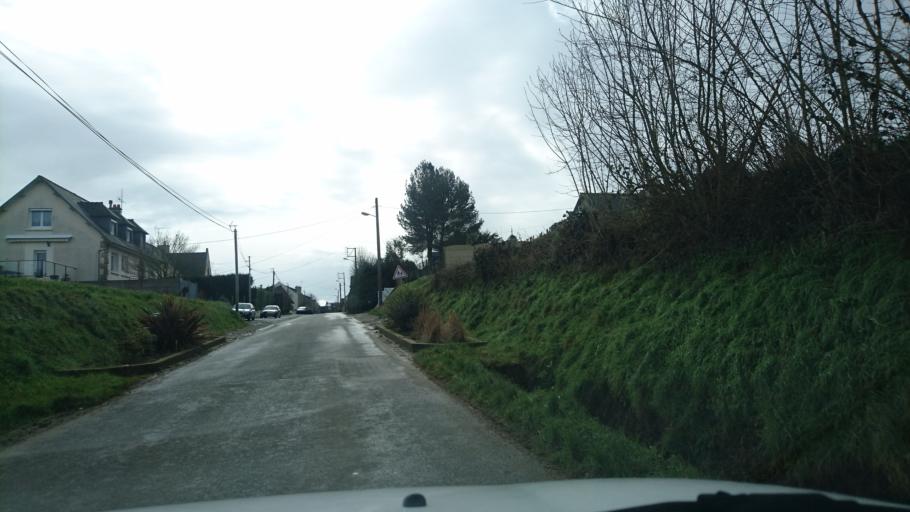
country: FR
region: Brittany
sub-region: Departement d'Ille-et-Vilaine
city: Antrain
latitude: 48.4642
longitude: -1.4876
